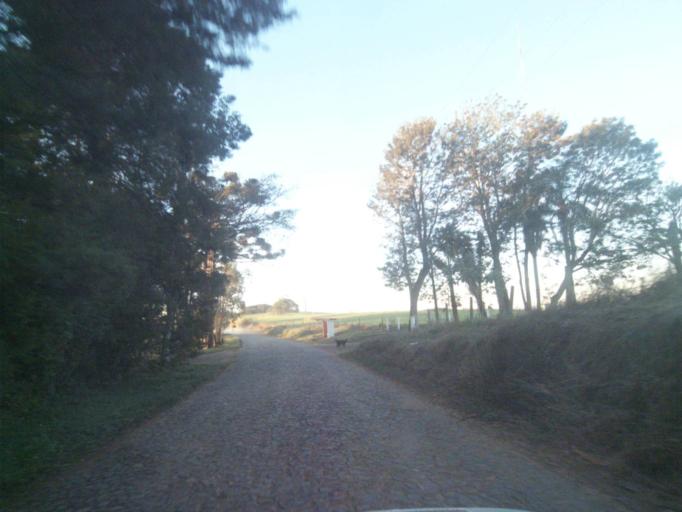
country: BR
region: Parana
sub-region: Tibagi
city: Tibagi
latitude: -24.5304
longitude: -50.4578
